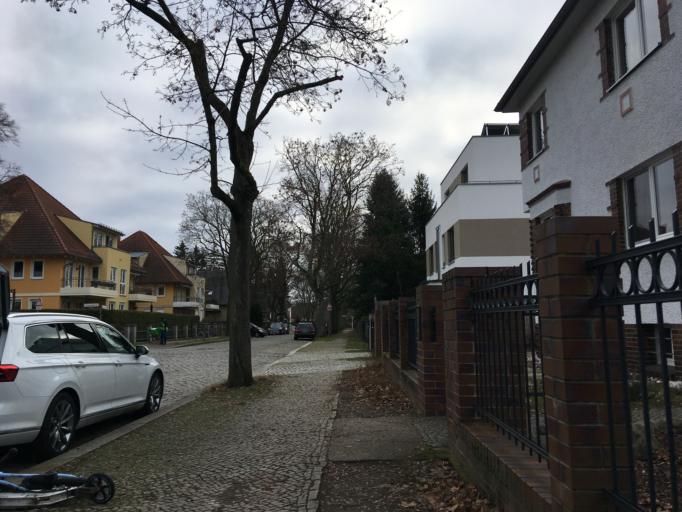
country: DE
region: Berlin
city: Niederschonhausen
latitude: 52.5811
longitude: 13.3889
